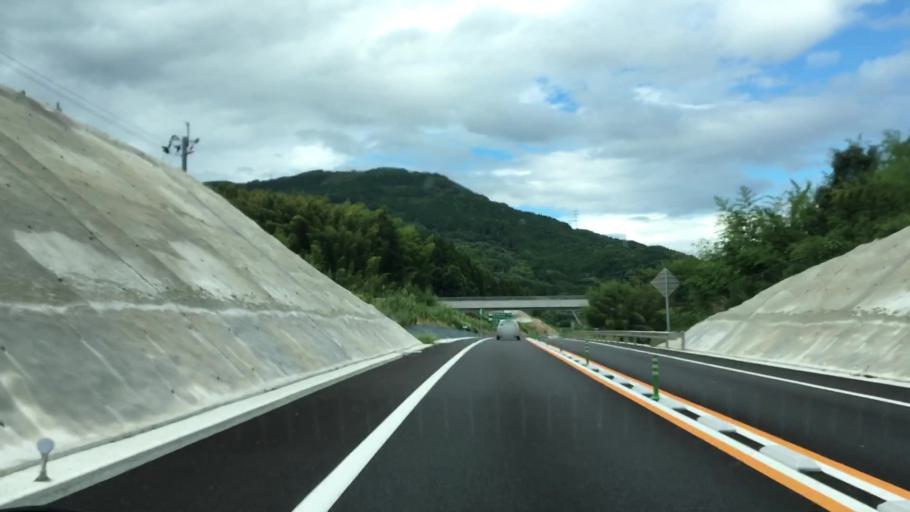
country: JP
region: Saga Prefecture
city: Imaricho-ko
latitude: 33.3073
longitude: 129.9162
